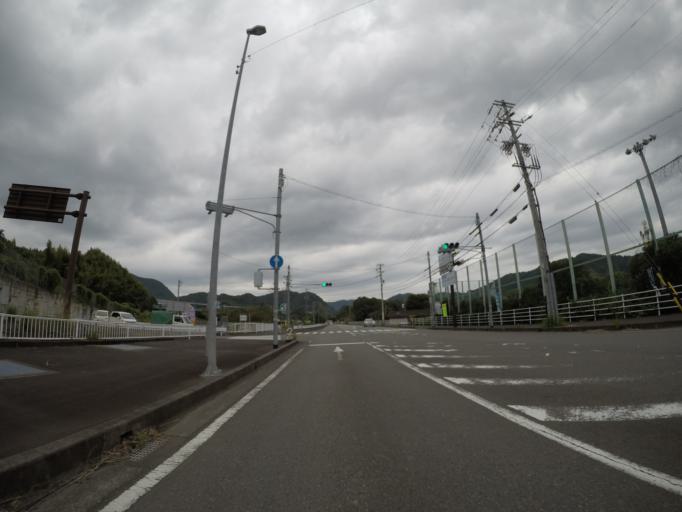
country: JP
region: Shizuoka
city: Fujieda
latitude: 34.9102
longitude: 138.2637
